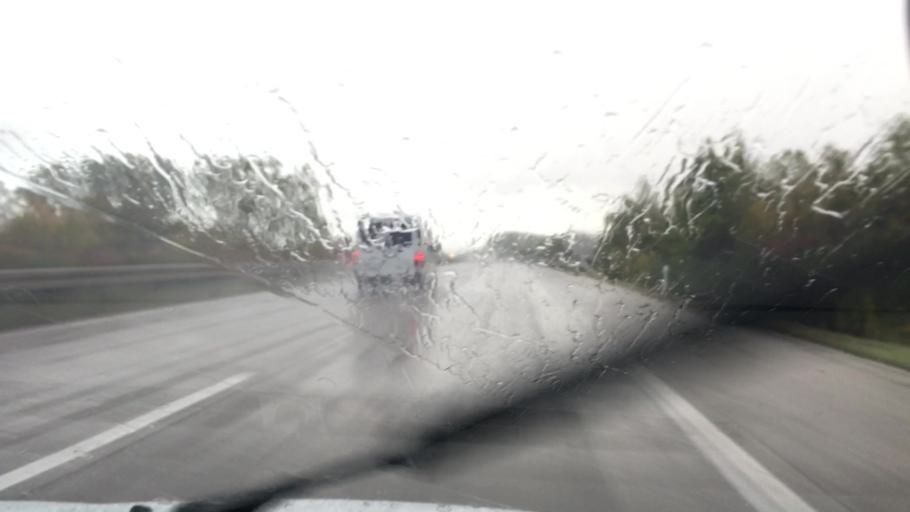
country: DE
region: Saxony-Anhalt
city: Biere
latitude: 51.9704
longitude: 11.6723
